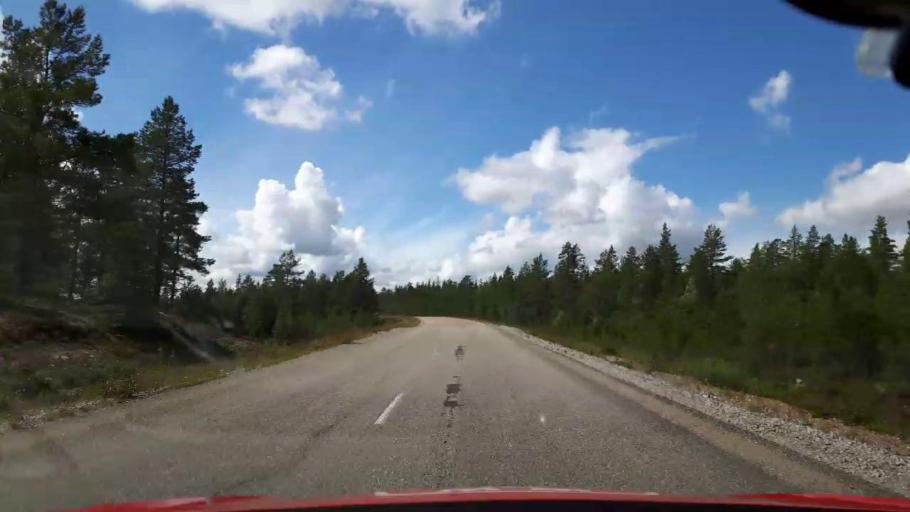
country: SE
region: Dalarna
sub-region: Alvdalens Kommun
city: AElvdalen
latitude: 61.8165
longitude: 13.5454
